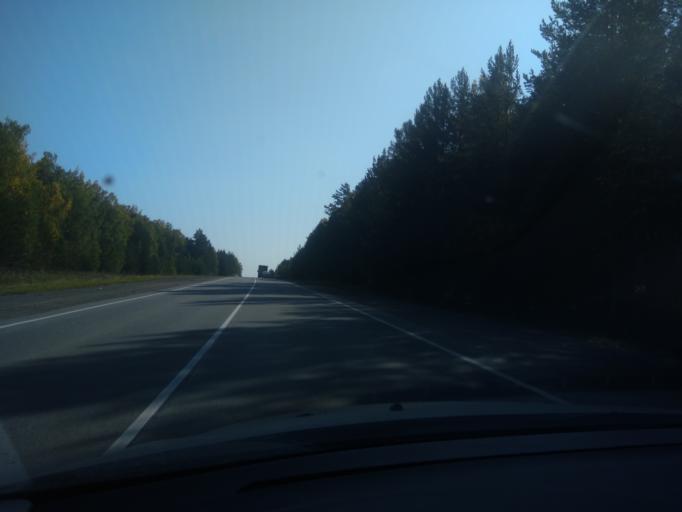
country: RU
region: Sverdlovsk
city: Verkhneye Dubrovo
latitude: 56.7052
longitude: 61.0733
